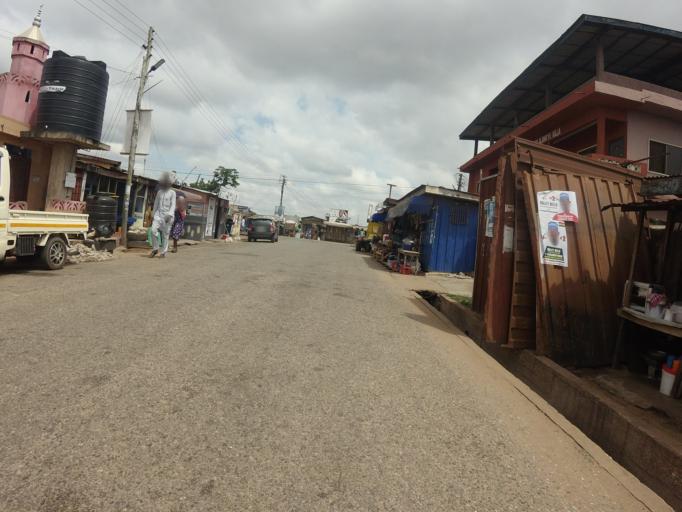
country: GH
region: Greater Accra
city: Accra
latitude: 5.5862
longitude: -0.2061
